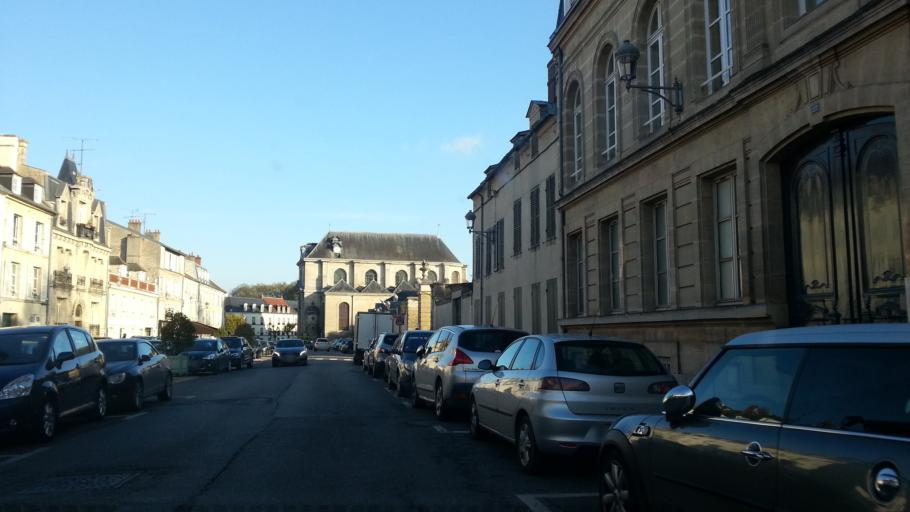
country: FR
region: Picardie
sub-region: Departement de l'Oise
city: Chantilly
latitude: 49.1945
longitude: 2.4765
